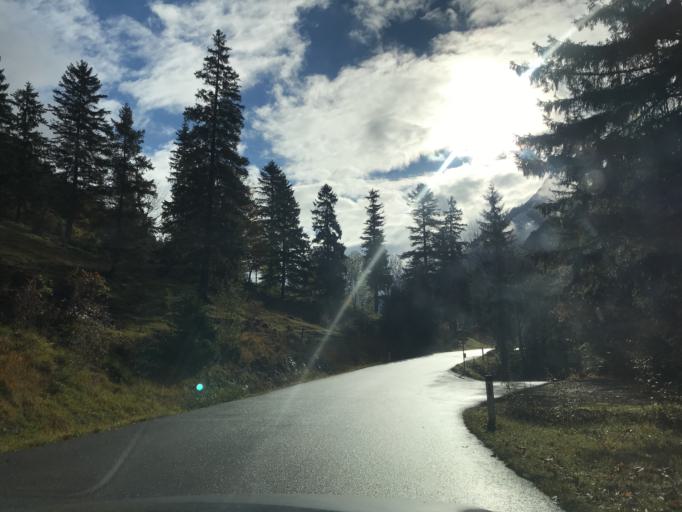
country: DE
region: Bavaria
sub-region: Upper Bavaria
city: Jachenau
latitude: 47.4632
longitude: 11.5020
